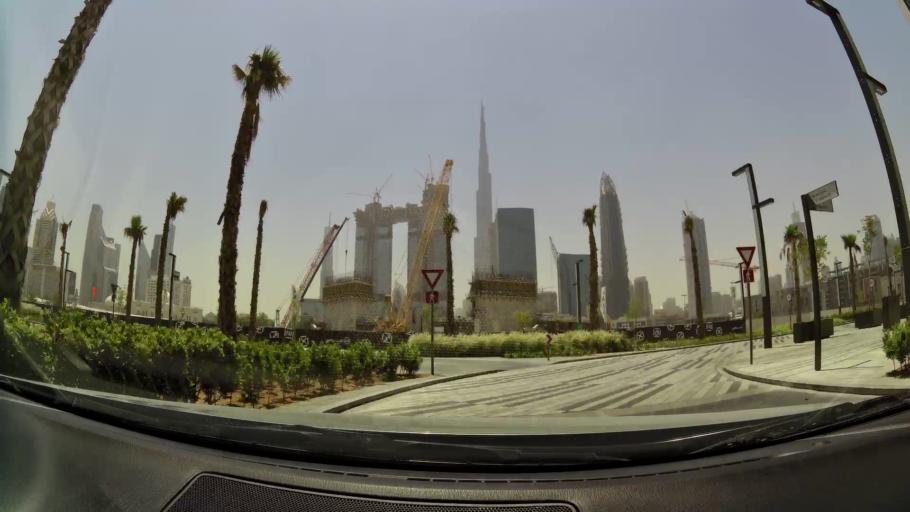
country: AE
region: Dubai
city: Dubai
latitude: 25.2049
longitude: 55.2643
